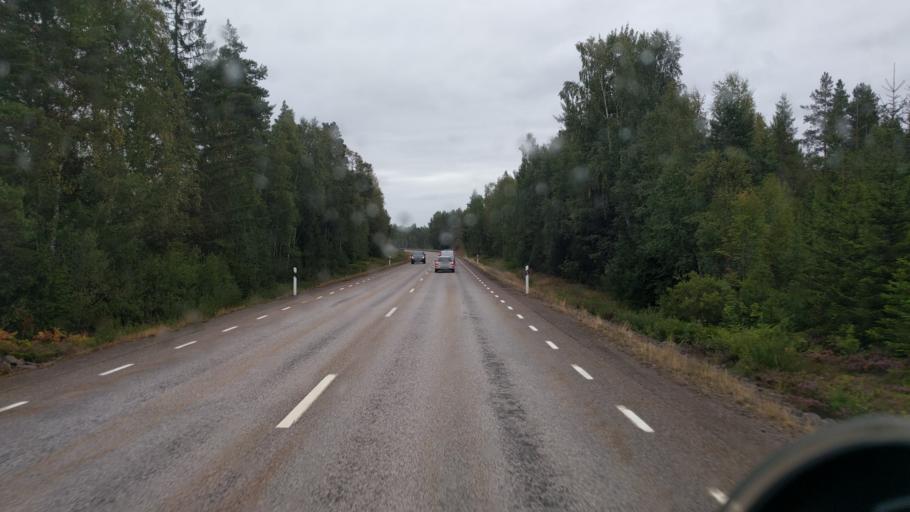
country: SE
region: Kalmar
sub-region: Vasterviks Kommun
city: Ankarsrum
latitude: 57.7024
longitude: 16.2181
